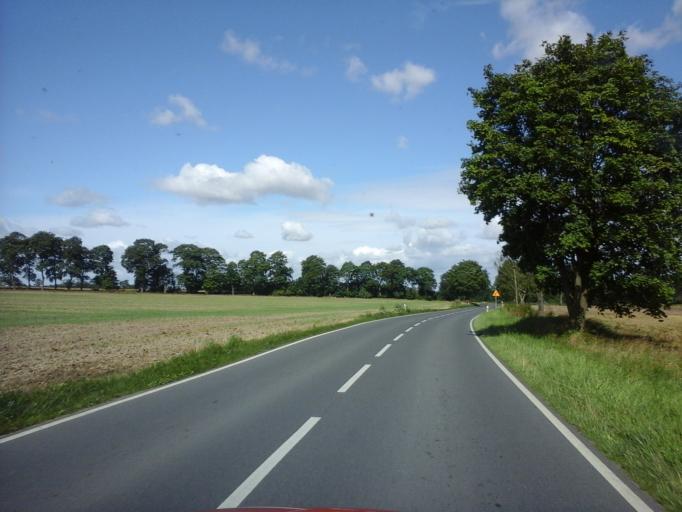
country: PL
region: West Pomeranian Voivodeship
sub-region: Powiat stargardzki
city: Dolice
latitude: 53.2036
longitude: 15.1507
